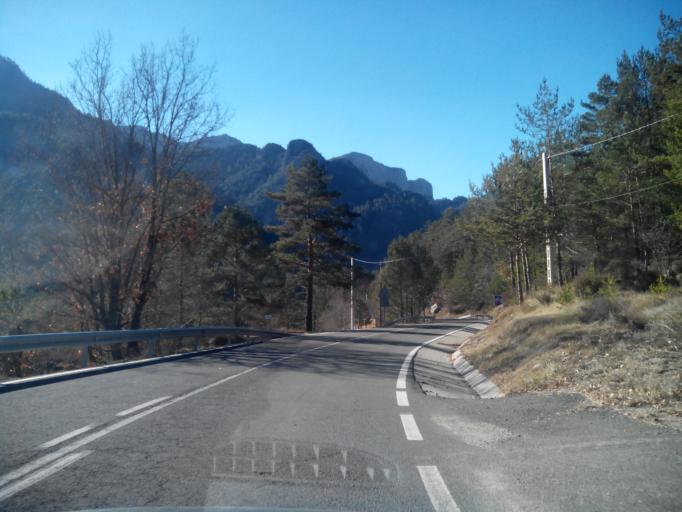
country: ES
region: Catalonia
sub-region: Provincia de Barcelona
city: Capolat
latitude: 42.1284
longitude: 1.6642
